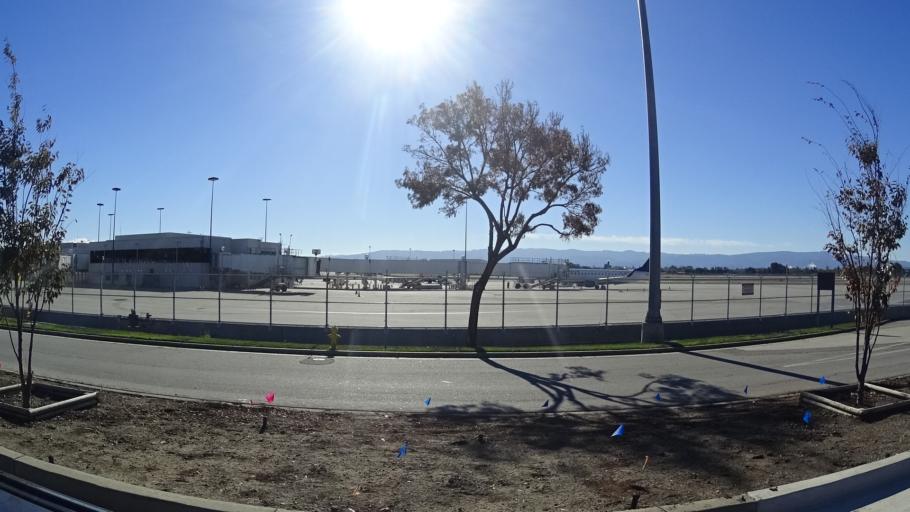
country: US
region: California
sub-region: Santa Clara County
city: Santa Clara
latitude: 37.3724
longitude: -121.9316
